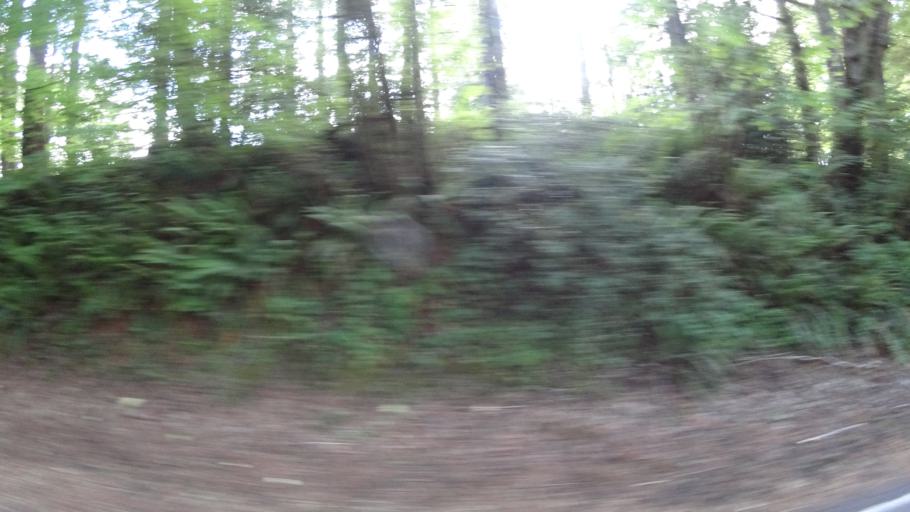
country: US
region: Oregon
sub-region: Washington County
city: Cedar Mill
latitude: 45.5806
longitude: -122.7982
